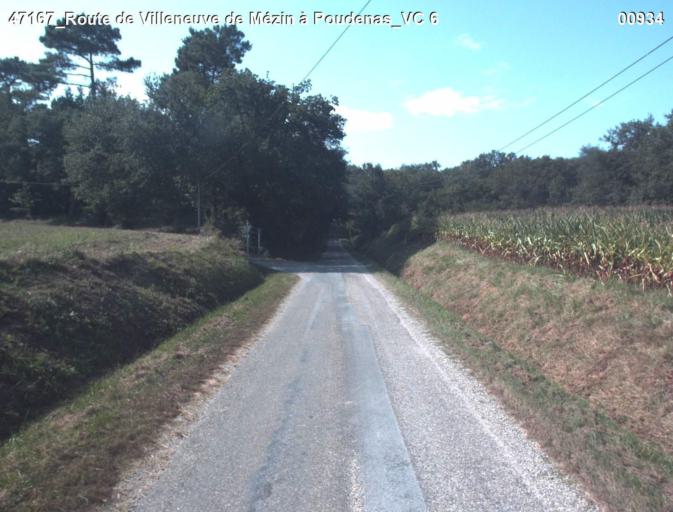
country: FR
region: Aquitaine
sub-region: Departement du Lot-et-Garonne
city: Mezin
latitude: 44.0335
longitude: 0.2276
